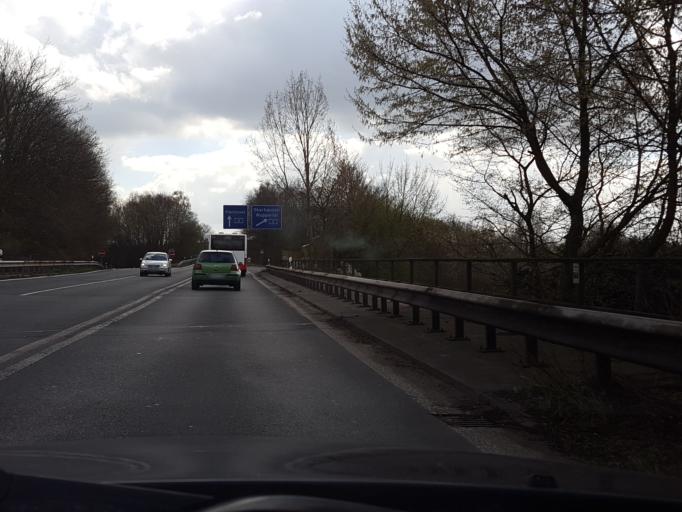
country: DE
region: North Rhine-Westphalia
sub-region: Regierungsbezirk Munster
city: Recklinghausen
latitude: 51.5879
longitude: 7.2152
